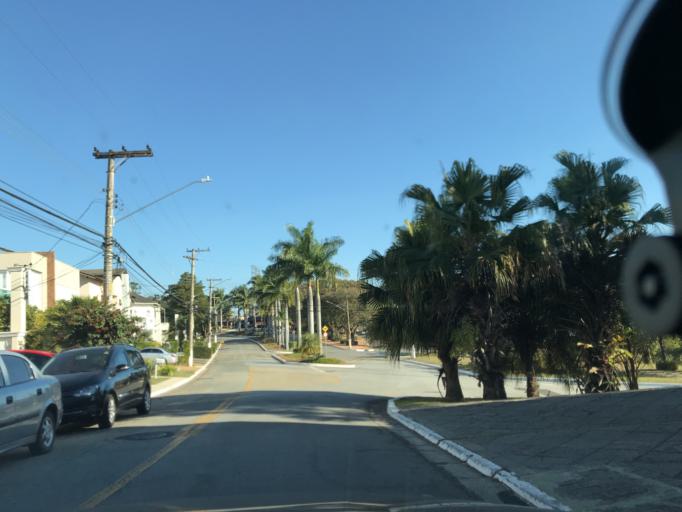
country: BR
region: Sao Paulo
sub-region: Santana De Parnaiba
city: Santana de Parnaiba
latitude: -23.4558
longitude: -46.8860
